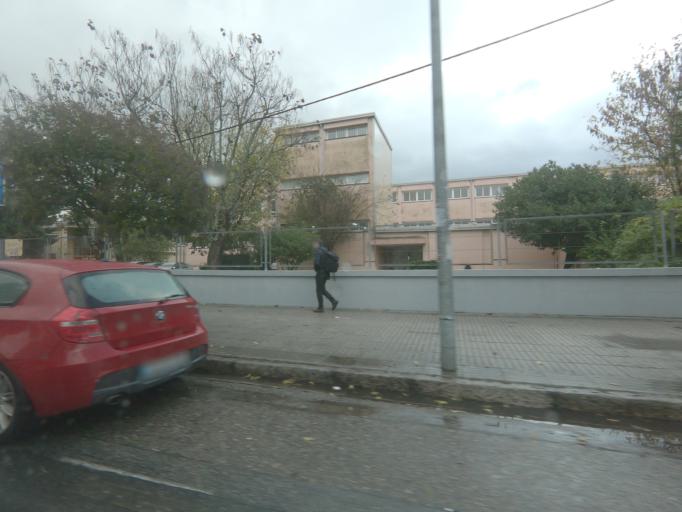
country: ES
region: Galicia
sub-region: Provincia de Pontevedra
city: Pontevedra
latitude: 42.4381
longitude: -8.6395
